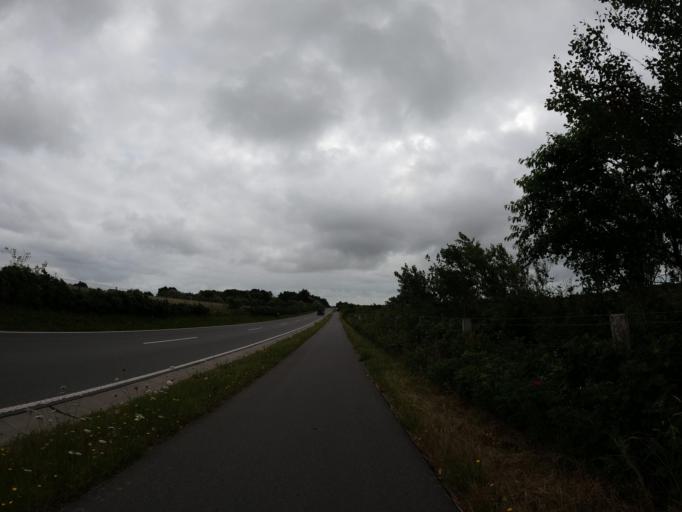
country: DE
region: Schleswig-Holstein
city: Keitum
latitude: 54.9249
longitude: 8.3578
